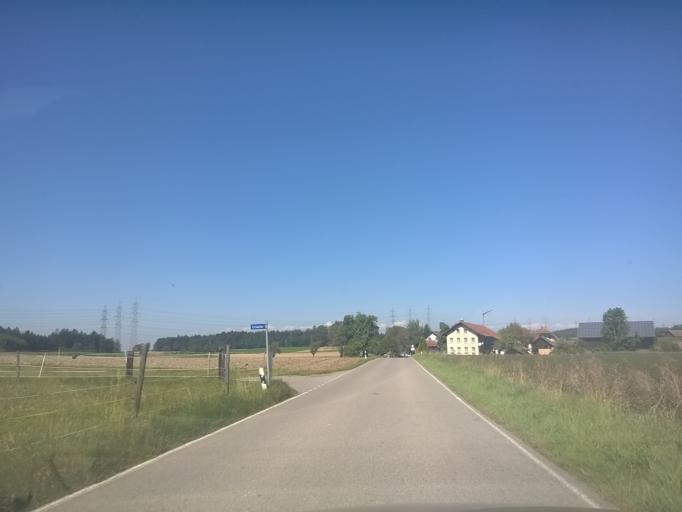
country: CH
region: Zurich
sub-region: Bezirk Winterthur
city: Brutten
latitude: 47.4812
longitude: 8.6609
